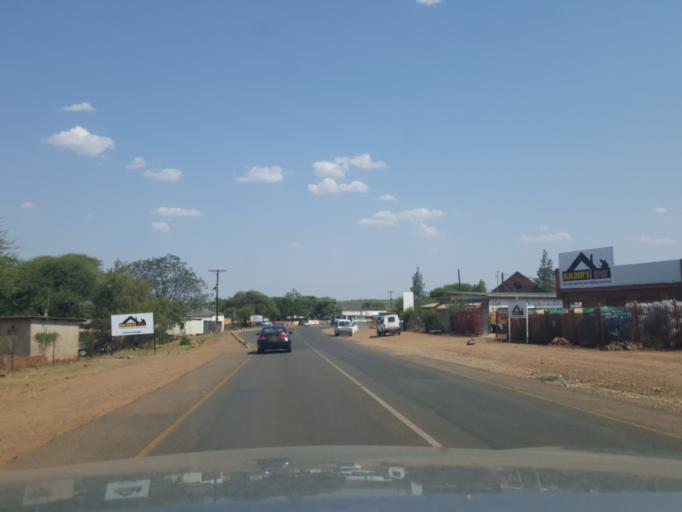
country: BW
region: South East
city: Ramotswa
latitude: -24.8473
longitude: 25.8297
